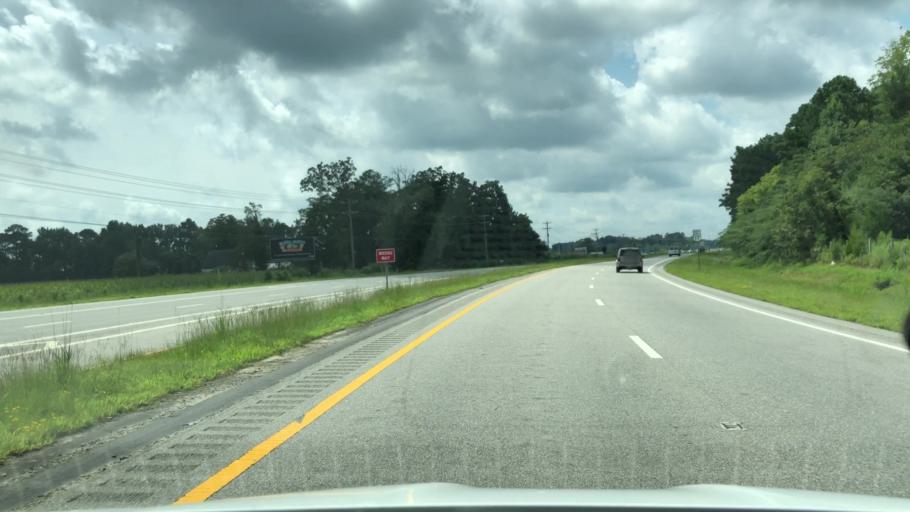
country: US
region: North Carolina
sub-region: Beaufort County
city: Washington
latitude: 35.4890
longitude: -77.1080
